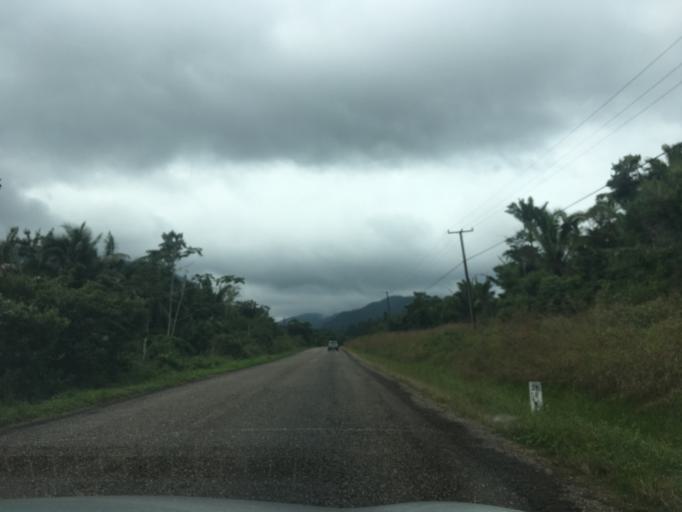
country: BZ
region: Cayo
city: Belmopan
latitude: 17.0493
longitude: -88.5483
